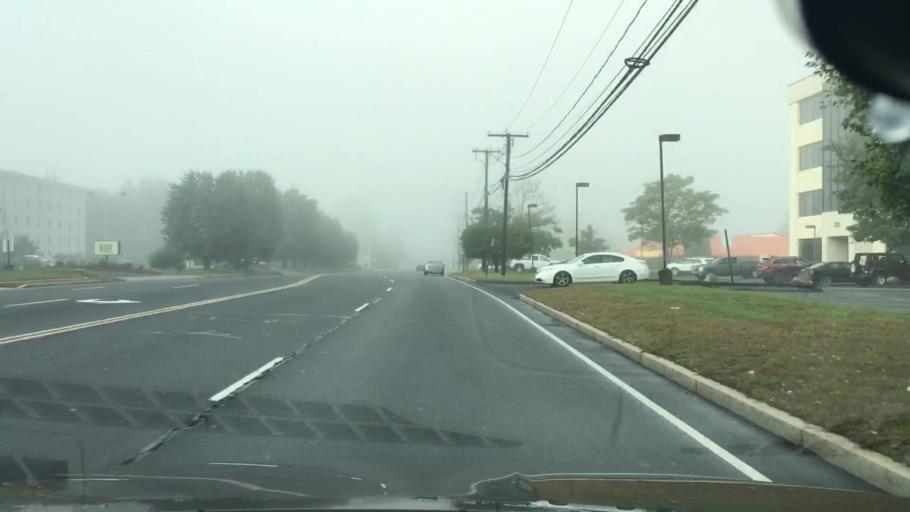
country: US
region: Connecticut
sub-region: Hartford County
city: East Hartford
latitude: 41.7690
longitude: -72.6199
